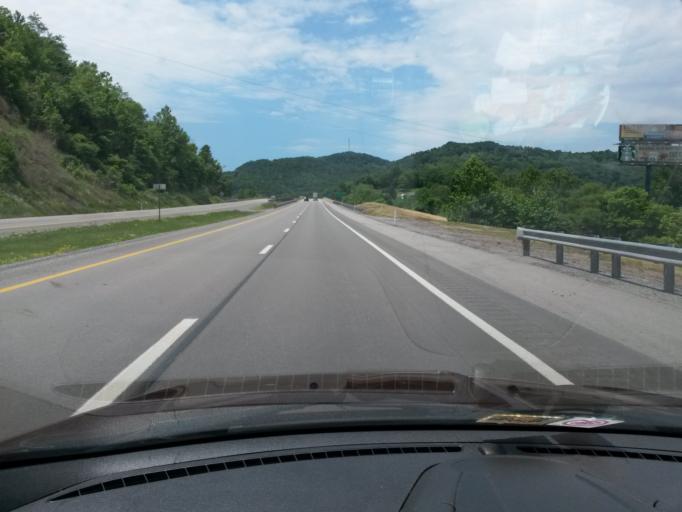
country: US
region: West Virginia
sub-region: Gilmer County
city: Glenville
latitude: 38.8630
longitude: -80.6525
